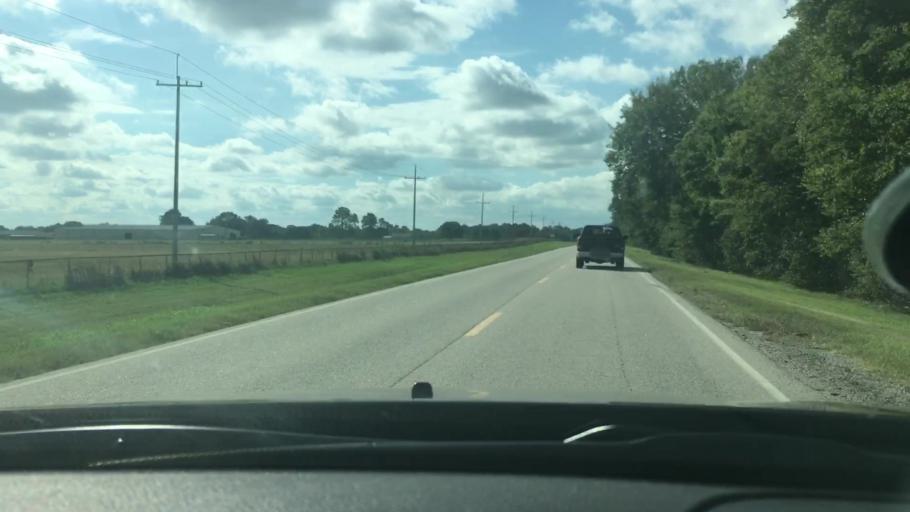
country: US
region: Oklahoma
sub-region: Pontotoc County
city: Ada
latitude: 34.6942
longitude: -96.6349
